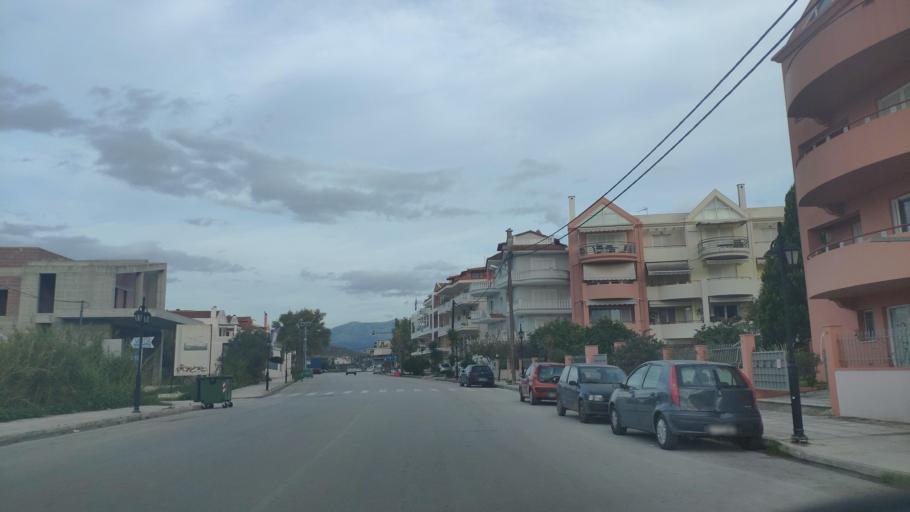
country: GR
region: Peloponnese
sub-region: Nomos Argolidos
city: Nafplio
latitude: 37.5736
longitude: 22.8038
